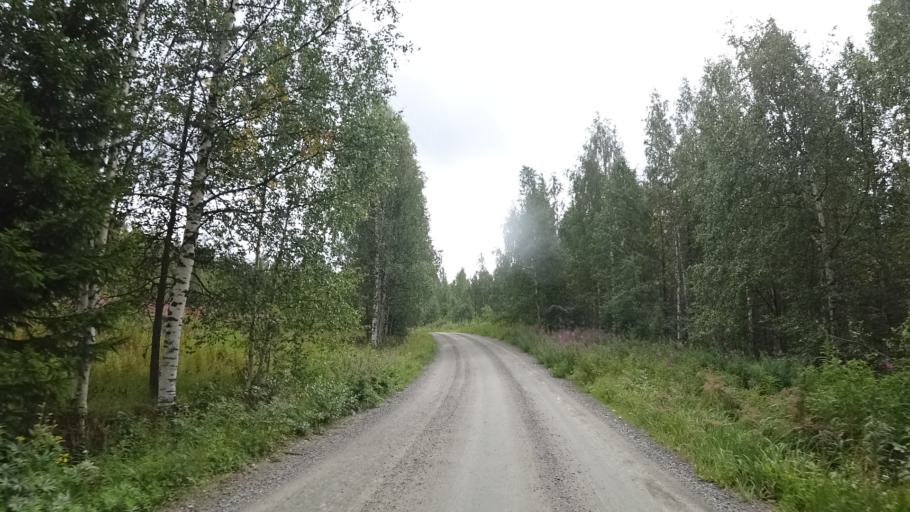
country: FI
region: North Karelia
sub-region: Joensuu
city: Ilomantsi
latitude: 62.9324
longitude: 31.3077
